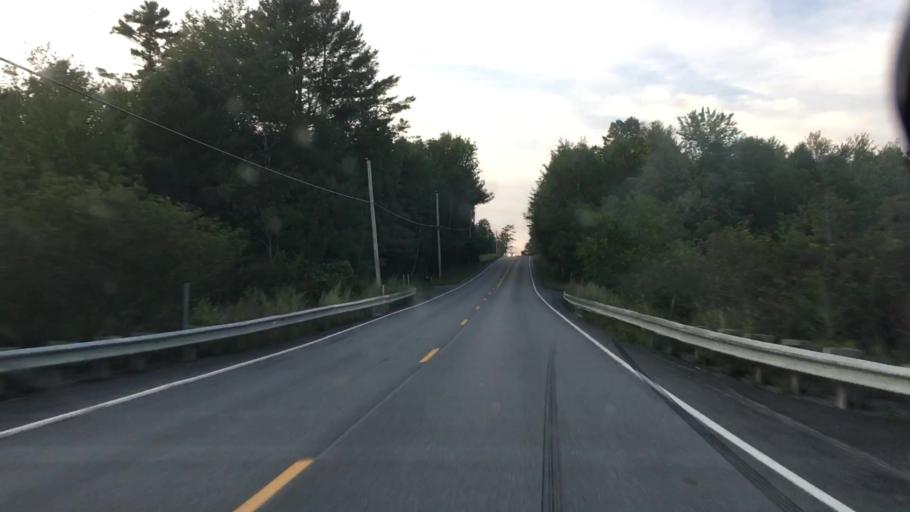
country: US
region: Maine
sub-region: Penobscot County
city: Hermon
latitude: 44.7507
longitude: -68.9701
